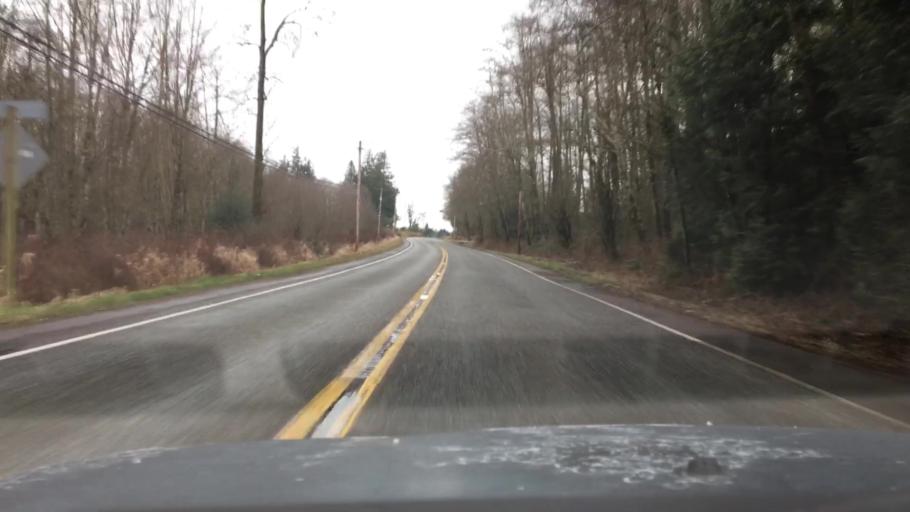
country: US
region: Washington
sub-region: Whatcom County
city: Sudden Valley
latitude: 48.6550
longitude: -122.3247
